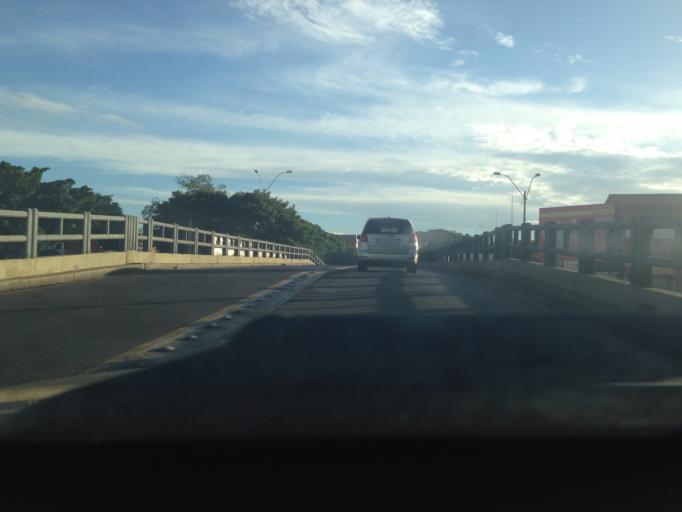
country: PY
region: Central
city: Lambare
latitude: -25.3116
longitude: -57.5869
